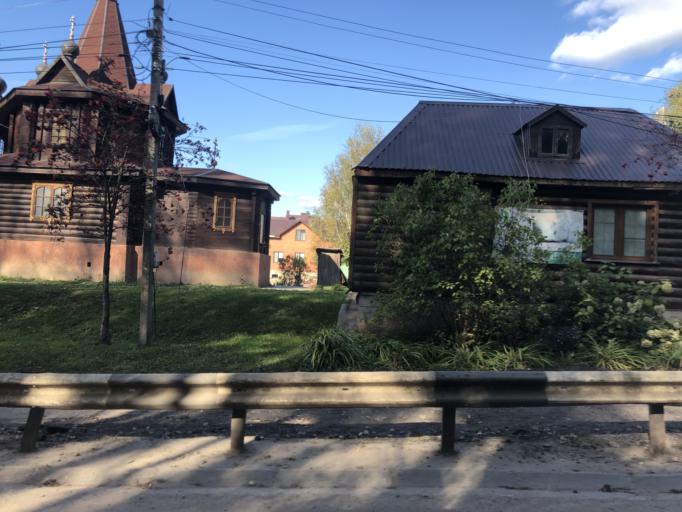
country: RU
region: Tverskaya
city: Rzhev
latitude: 56.2621
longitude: 34.3456
